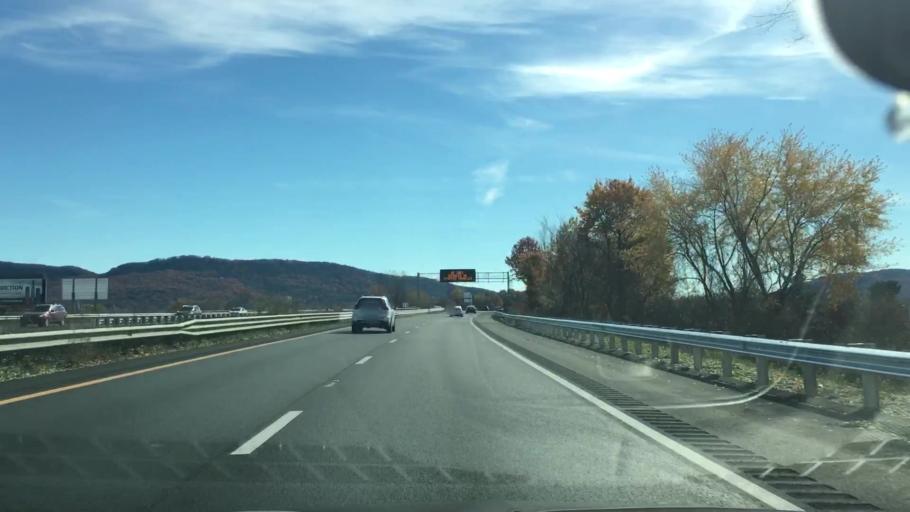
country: US
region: Massachusetts
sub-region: Hampshire County
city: Northampton
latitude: 42.3287
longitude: -72.6176
